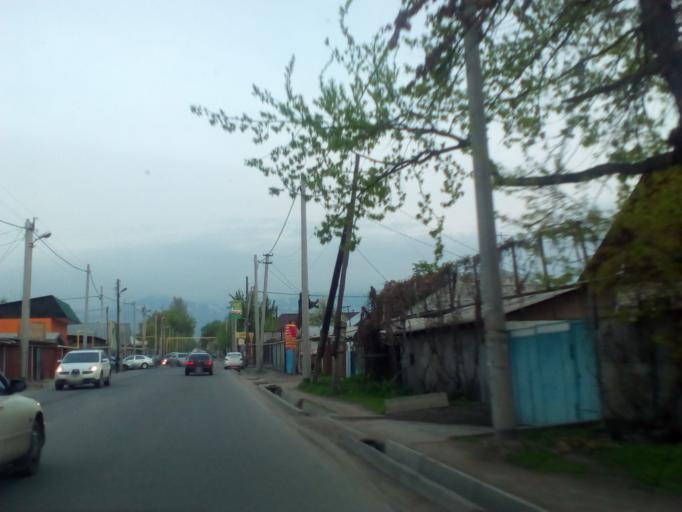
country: KZ
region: Almaty Qalasy
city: Almaty
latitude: 43.2331
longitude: 76.8256
